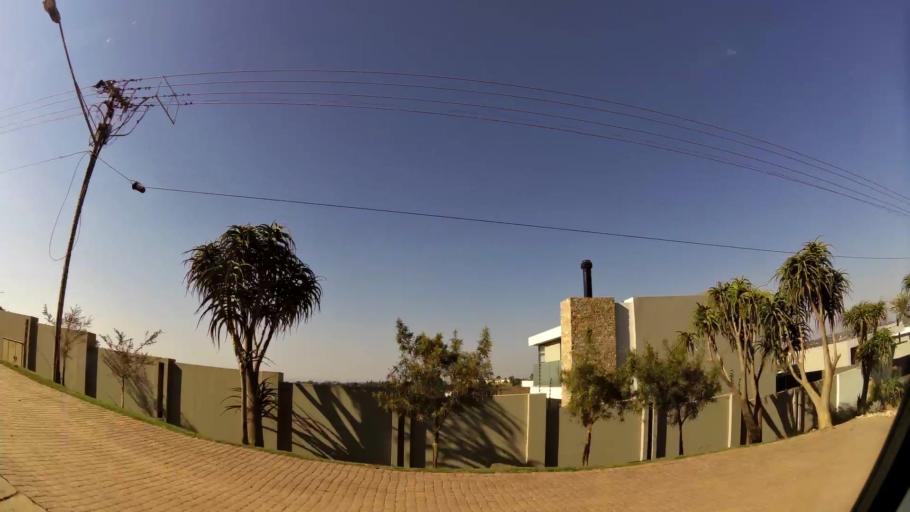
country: ZA
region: Gauteng
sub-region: City of Tshwane Metropolitan Municipality
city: Pretoria
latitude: -25.8003
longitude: 28.2455
